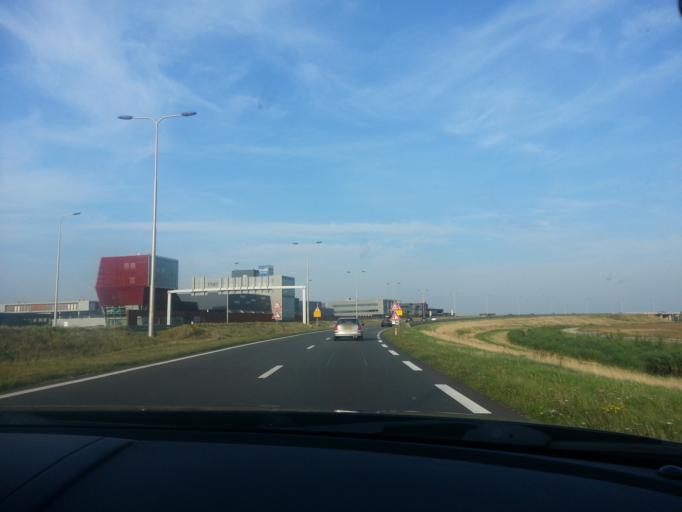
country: NL
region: South Holland
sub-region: Gemeente Kaag en Braassem
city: Oude Wetering
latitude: 52.2517
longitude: 4.6252
